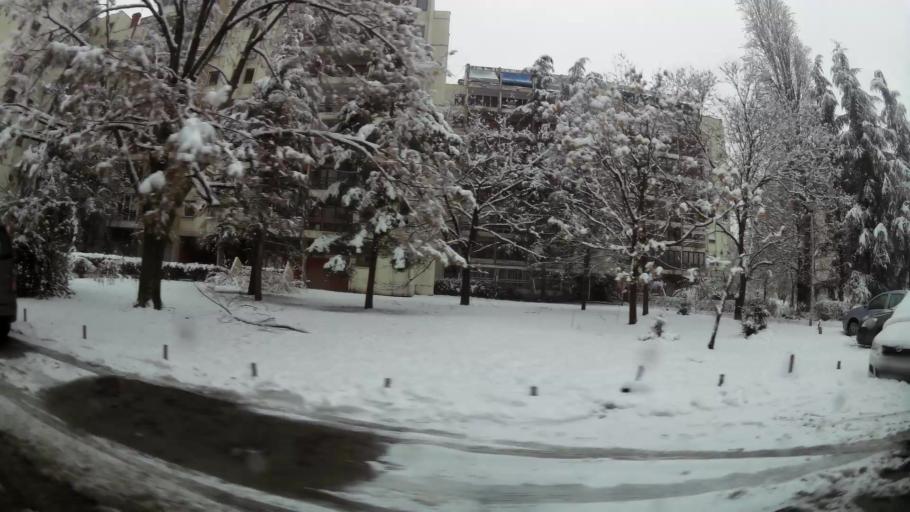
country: RS
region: Central Serbia
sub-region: Belgrade
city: Novi Beograd
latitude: 44.7992
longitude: 20.4039
